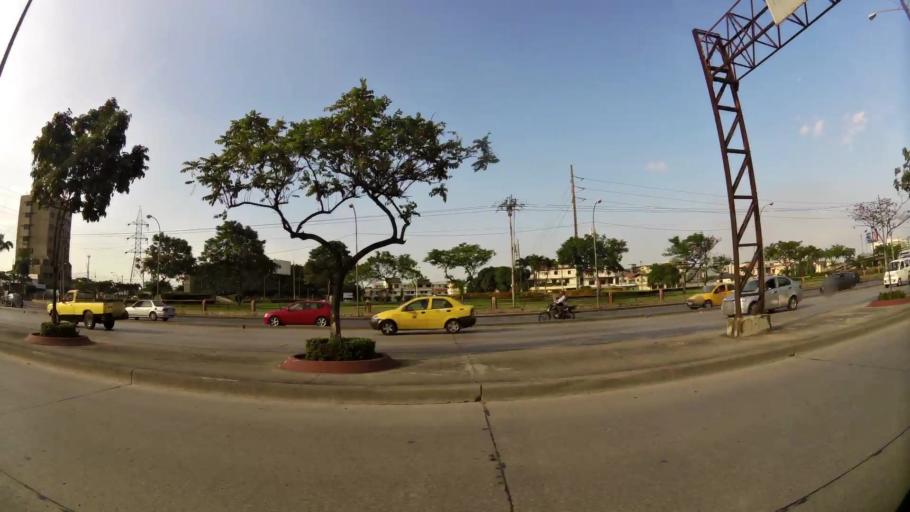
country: EC
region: Guayas
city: Eloy Alfaro
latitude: -2.1529
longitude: -79.8971
